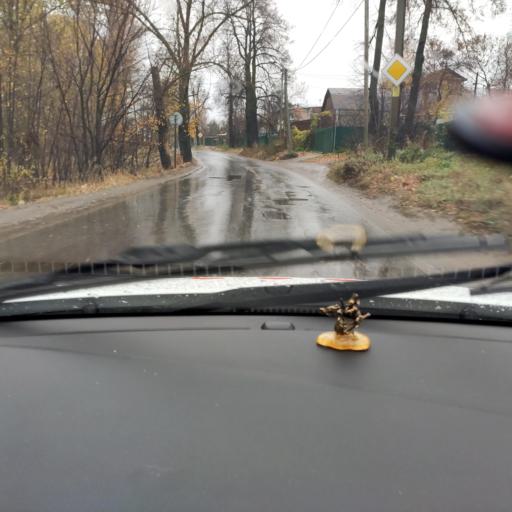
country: RU
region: Tatarstan
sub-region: Gorod Kazan'
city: Kazan
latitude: 55.7272
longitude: 49.1582
